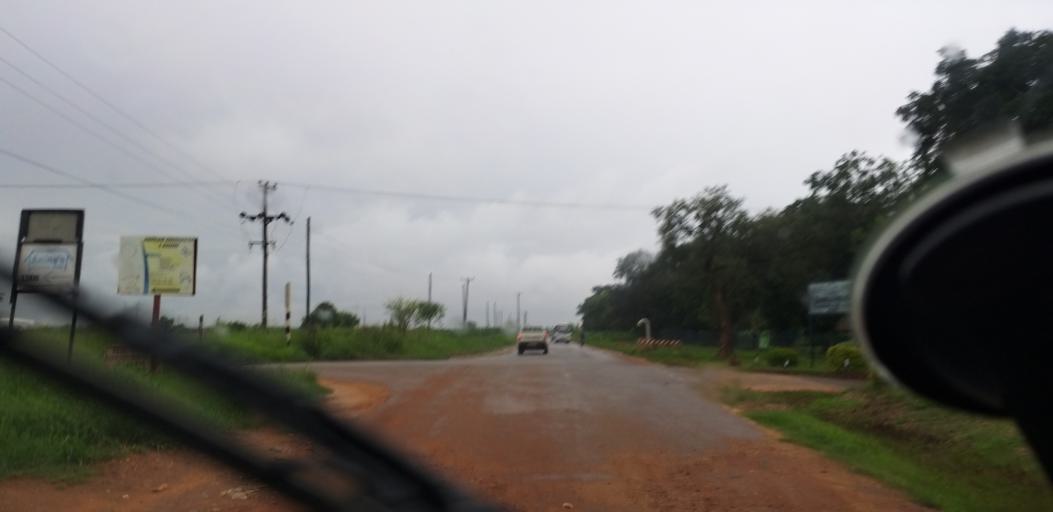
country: ZM
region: Lusaka
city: Lusaka
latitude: -15.5209
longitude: 28.2974
